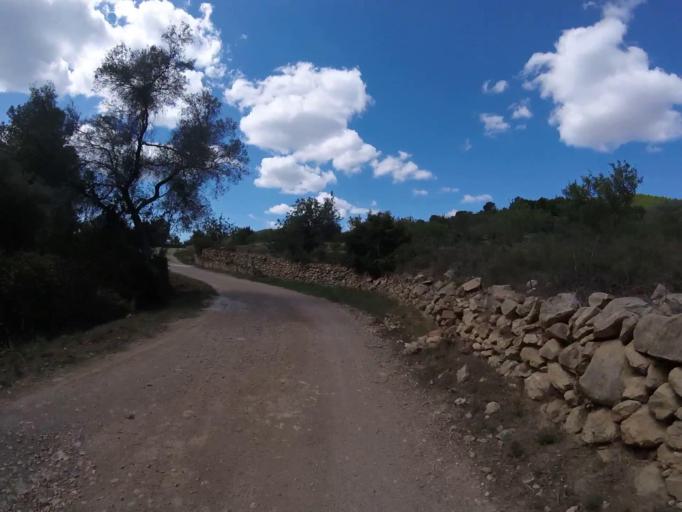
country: ES
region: Valencia
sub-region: Provincia de Castello
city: Santa Magdalena de Pulpis
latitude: 40.3156
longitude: 0.3304
